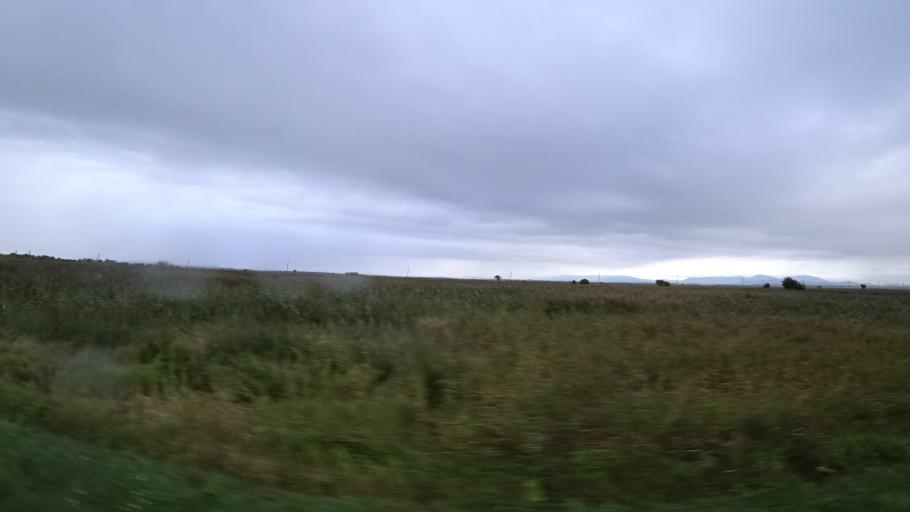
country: RU
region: Primorskiy
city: Chernigovka
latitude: 44.3907
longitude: 132.5291
